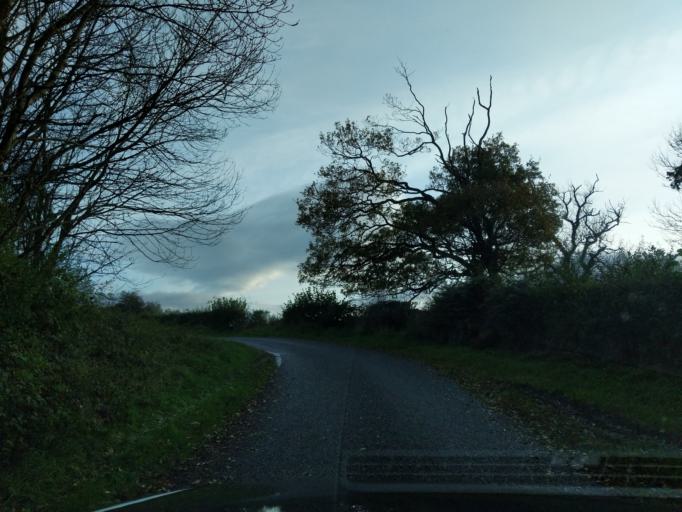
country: GB
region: Scotland
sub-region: Dumfries and Galloway
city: Kirkcudbright
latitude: 54.8399
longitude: -4.1803
